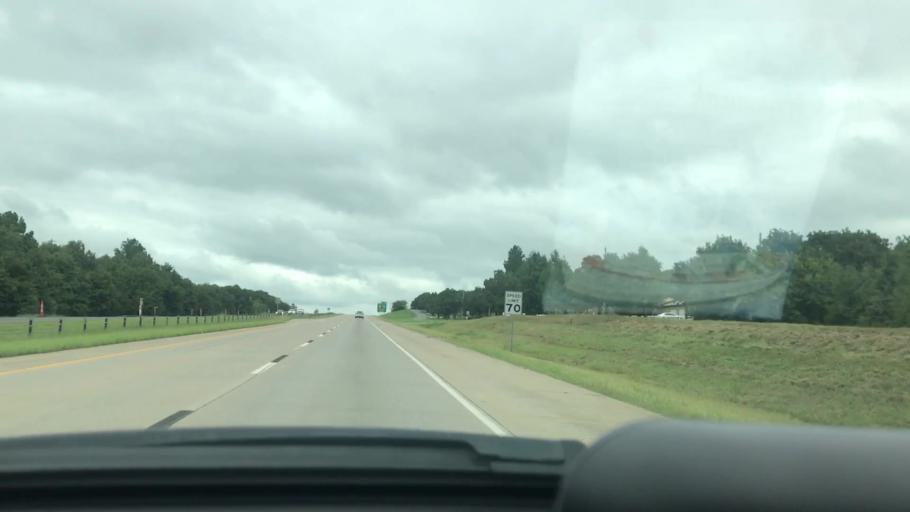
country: US
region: Oklahoma
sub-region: Pittsburg County
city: Krebs
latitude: 34.9842
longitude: -95.7223
